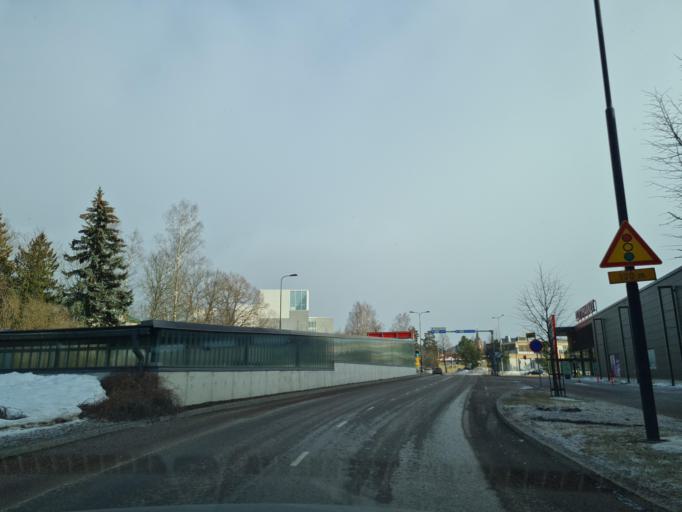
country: FI
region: Uusimaa
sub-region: Helsinki
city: Maentsaelae
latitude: 60.6381
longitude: 25.3173
